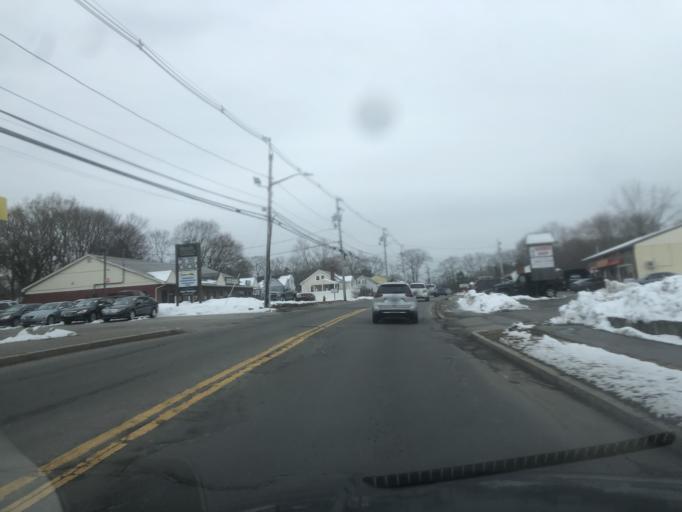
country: US
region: Massachusetts
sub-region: Middlesex County
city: Tewksbury
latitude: 42.6060
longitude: -71.2257
